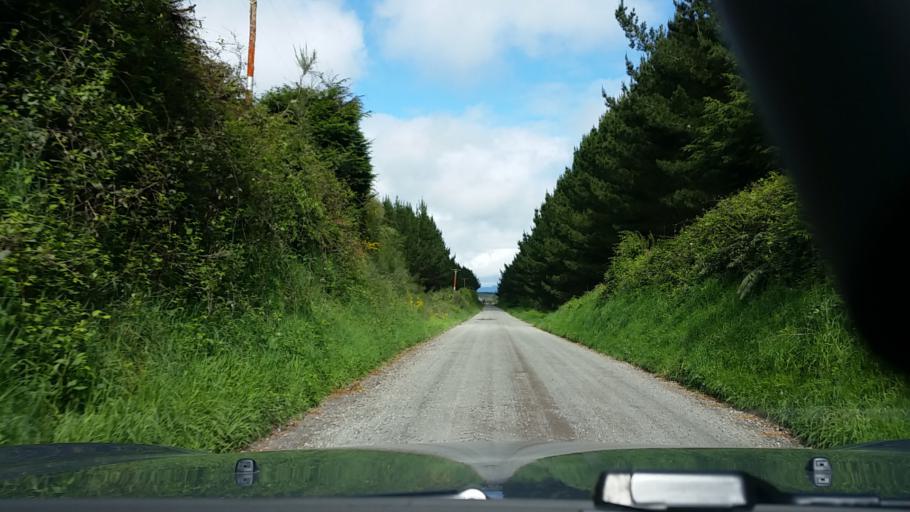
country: NZ
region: Bay of Plenty
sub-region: Whakatane District
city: Murupara
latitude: -38.3508
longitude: 176.4845
